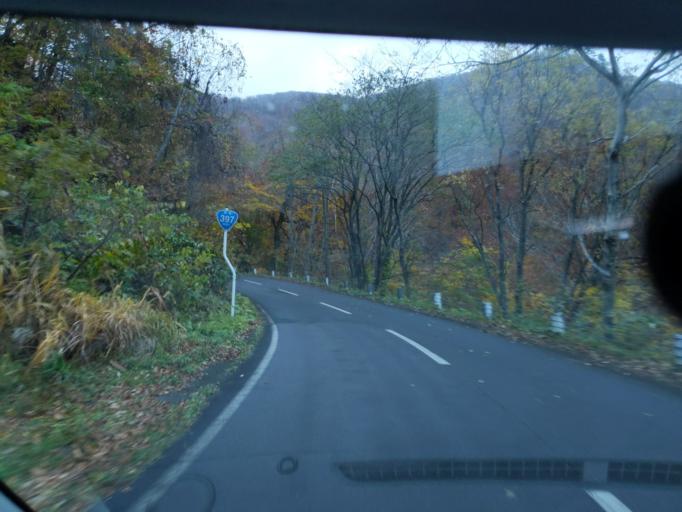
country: JP
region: Iwate
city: Mizusawa
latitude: 39.1158
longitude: 140.8409
